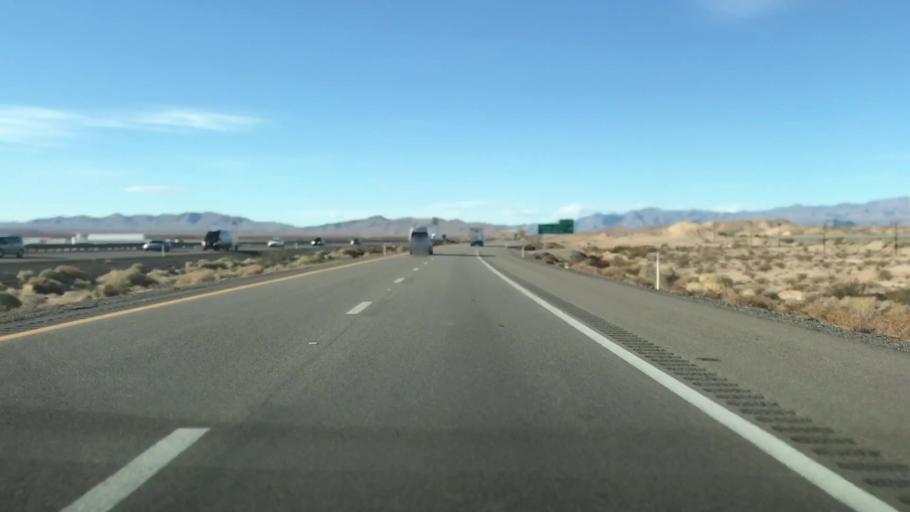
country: US
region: Nevada
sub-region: Clark County
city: Moapa Town
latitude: 36.5062
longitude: -114.7556
